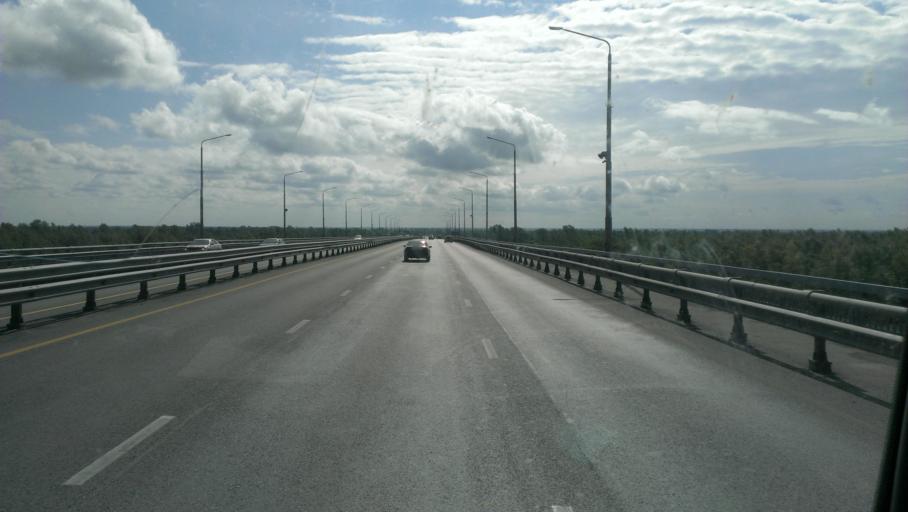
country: RU
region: Altai Krai
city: Zaton
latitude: 53.3229
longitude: 83.8046
